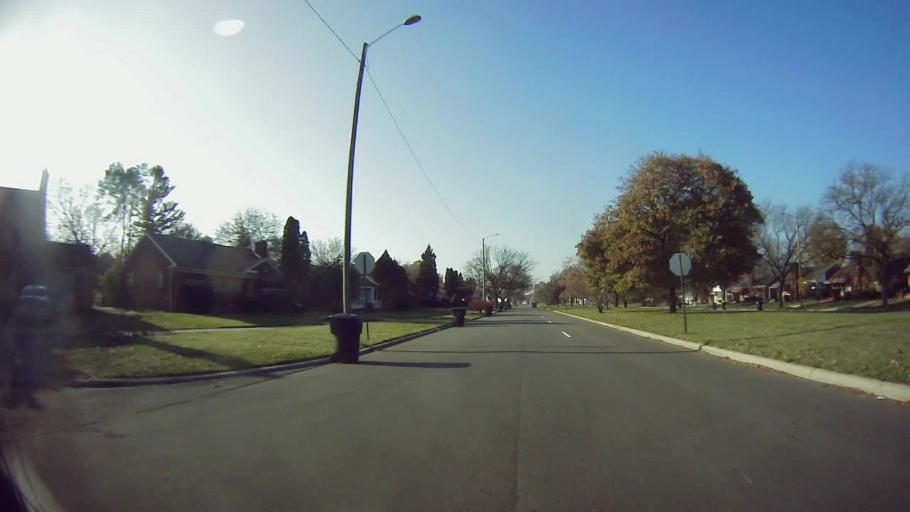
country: US
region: Michigan
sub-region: Wayne County
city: Dearborn
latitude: 42.3638
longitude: -83.1559
